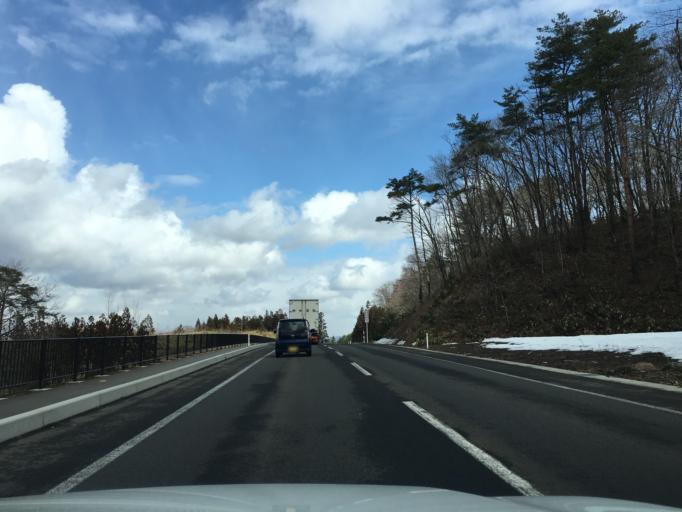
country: JP
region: Akita
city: Takanosu
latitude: 40.1049
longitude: 140.3502
